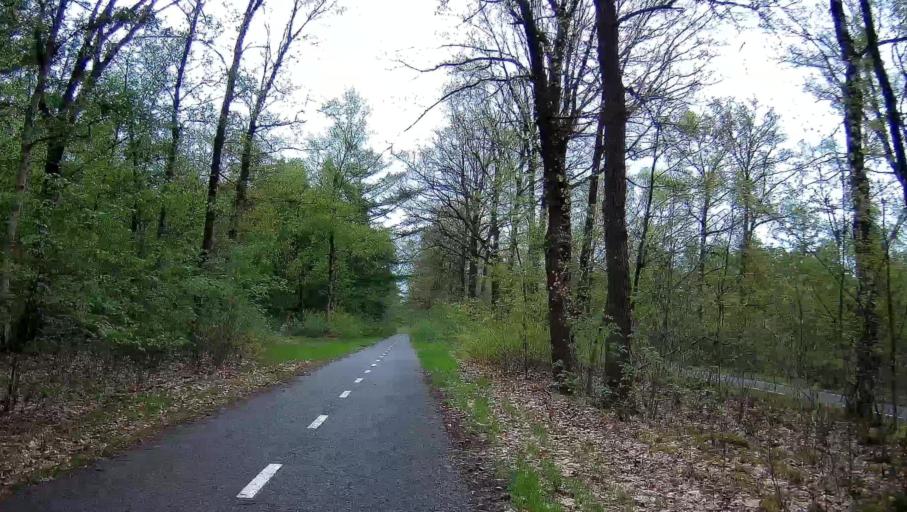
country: NL
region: Drenthe
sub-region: Gemeente Borger-Odoorn
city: Borger
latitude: 52.9480
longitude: 6.7086
